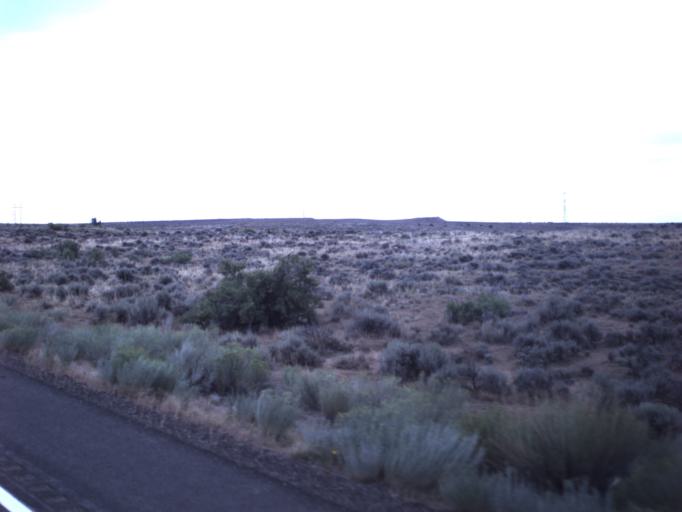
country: US
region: Utah
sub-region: Uintah County
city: Naples
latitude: 40.2240
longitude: -109.3938
